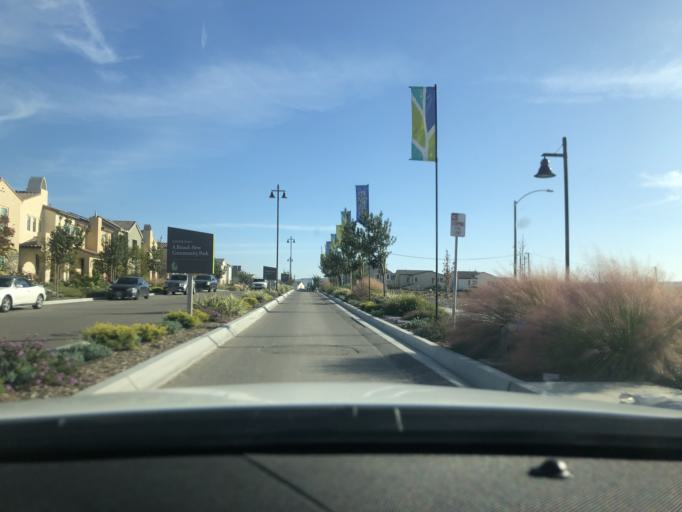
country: US
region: California
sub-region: San Diego County
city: Bonita
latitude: 32.5984
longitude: -117.0044
